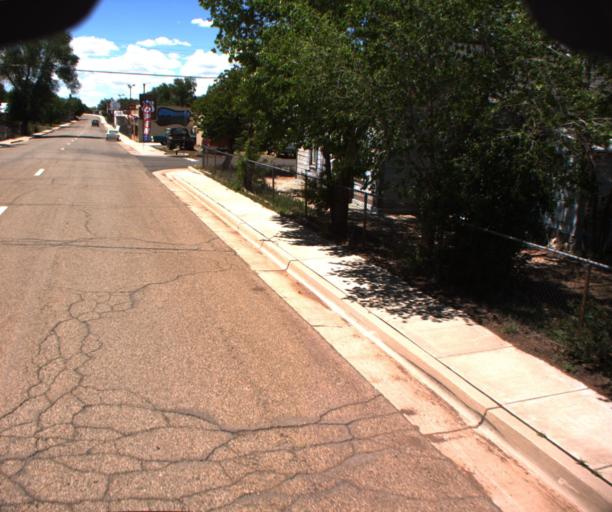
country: US
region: Arizona
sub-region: Coconino County
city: Williams
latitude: 35.2240
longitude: -112.4816
